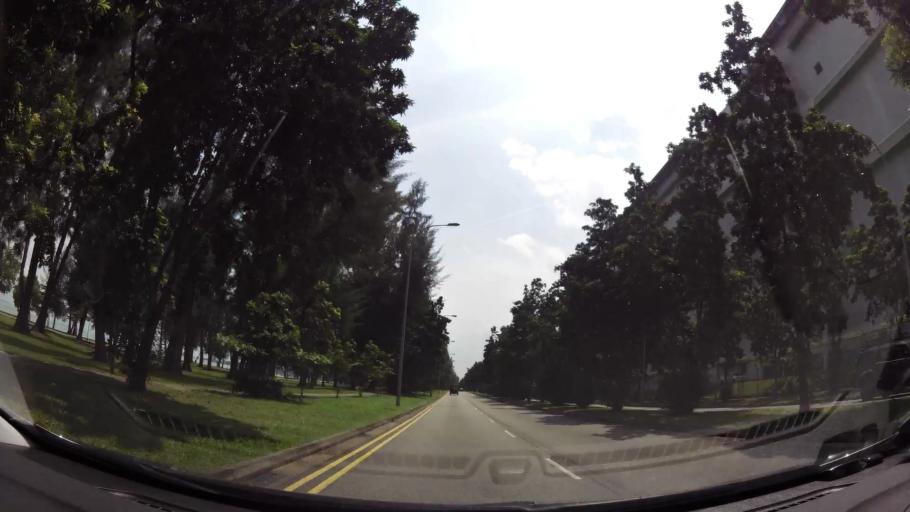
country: MY
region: Johor
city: Kampung Pasir Gudang Baru
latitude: 1.3809
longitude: 104.0020
